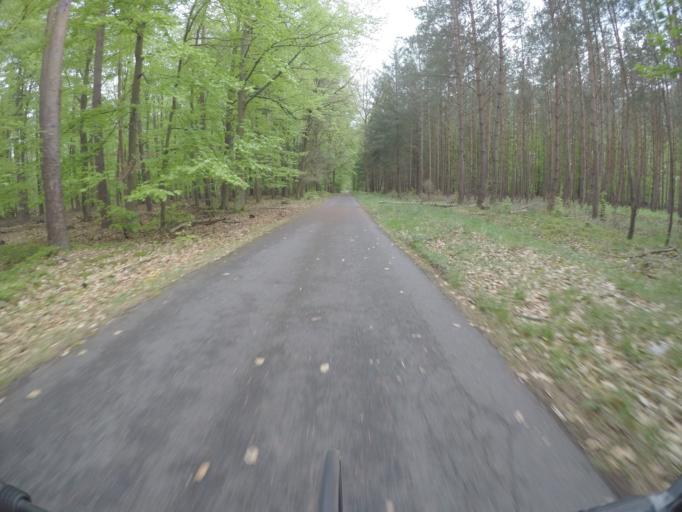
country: DE
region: Brandenburg
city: Biesenthal
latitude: 52.8074
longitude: 13.6313
